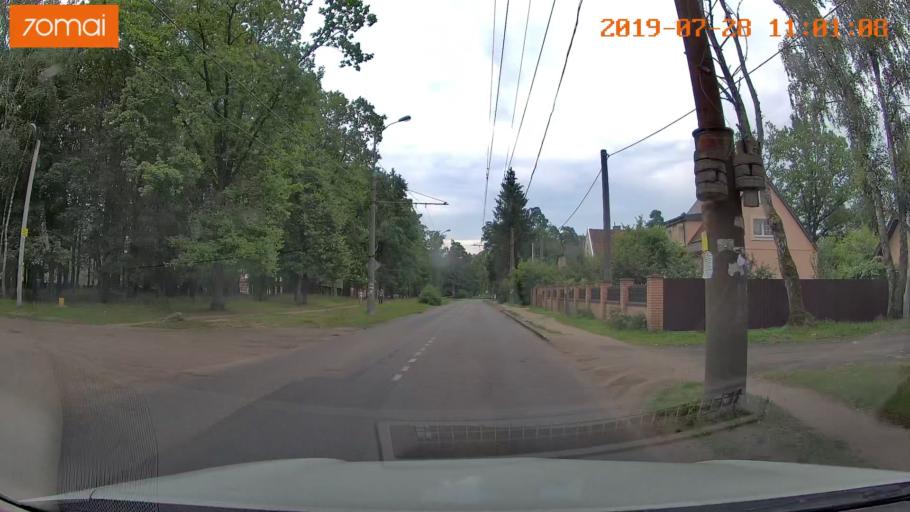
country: RU
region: Kaliningrad
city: Vzmorye
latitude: 54.7234
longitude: 20.3665
